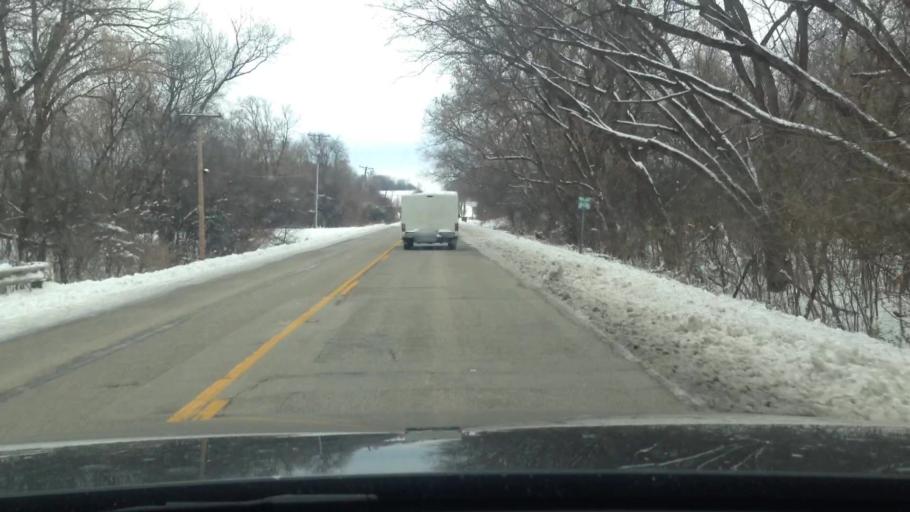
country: US
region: Illinois
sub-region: McHenry County
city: Hebron
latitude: 42.4837
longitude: -88.4425
